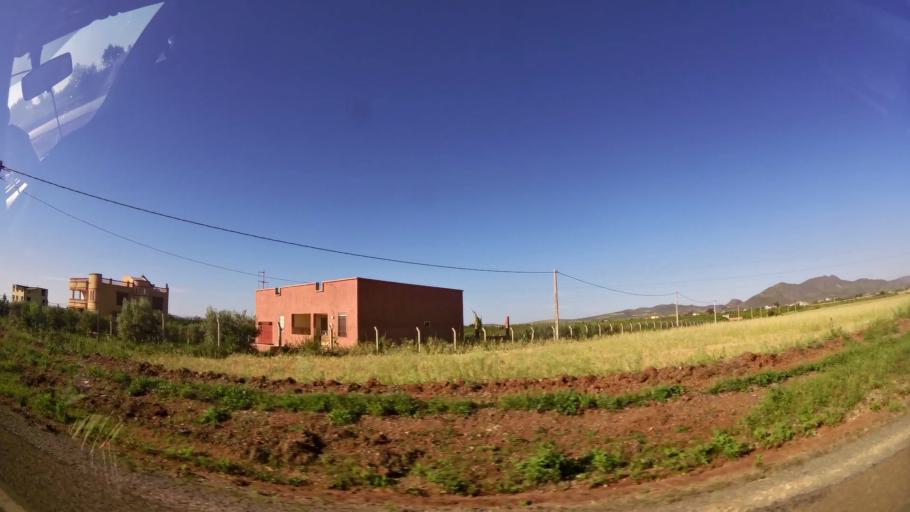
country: MA
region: Oriental
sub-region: Berkane-Taourirt
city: Ahfir
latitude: 34.9939
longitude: -2.1626
